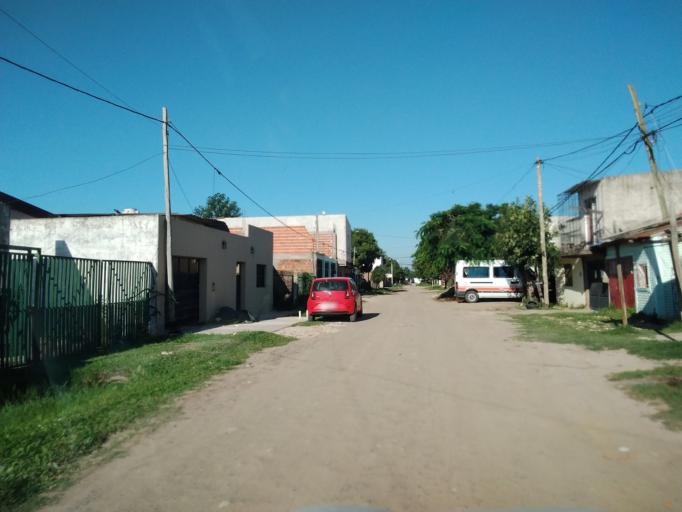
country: AR
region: Corrientes
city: Corrientes
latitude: -27.4857
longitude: -58.8144
